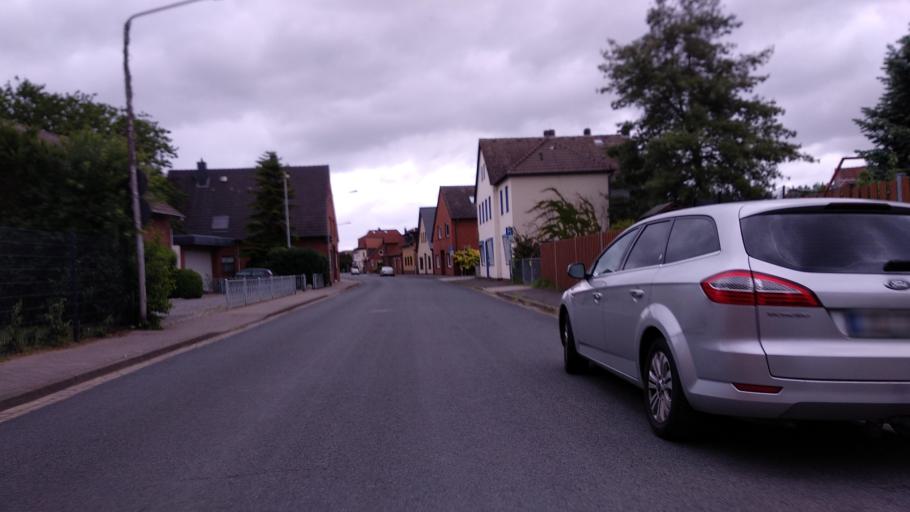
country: DE
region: Lower Saxony
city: Hagenburg
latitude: 52.4562
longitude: 9.3579
